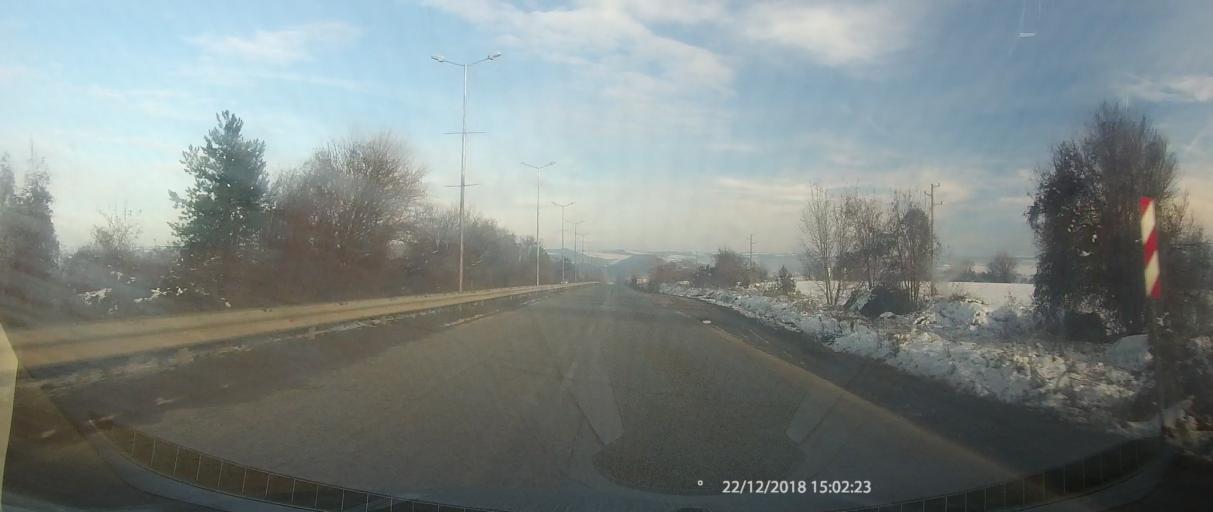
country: BG
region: Ruse
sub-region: Obshtina Tsenovo
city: Tsenovo
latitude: 43.4691
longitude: 25.6933
